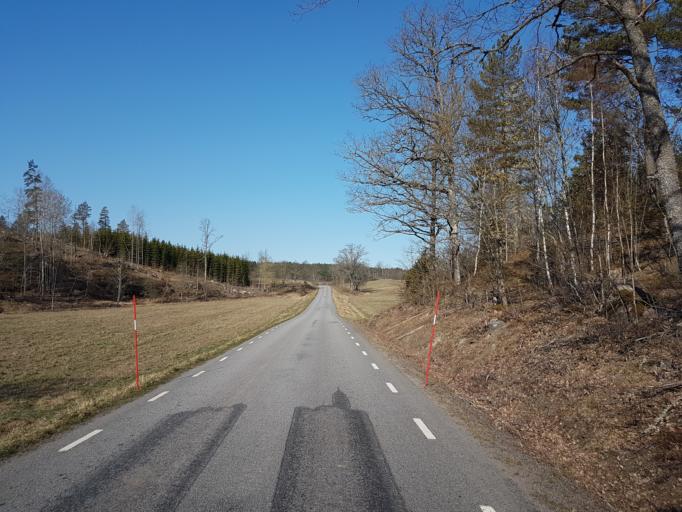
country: SE
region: OEstergoetland
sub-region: Valdemarsviks Kommun
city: Gusum
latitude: 58.1999
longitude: 16.3573
